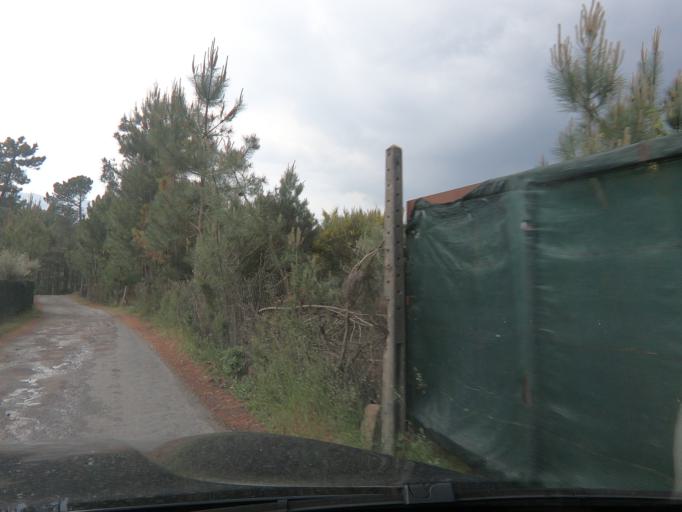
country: PT
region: Vila Real
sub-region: Vila Real
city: Vila Real
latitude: 41.3216
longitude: -7.6905
